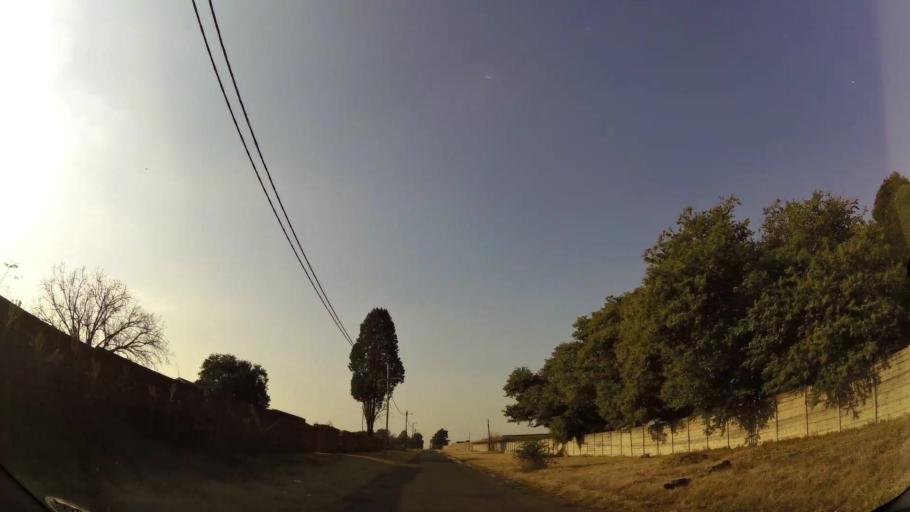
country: ZA
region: Gauteng
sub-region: Ekurhuleni Metropolitan Municipality
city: Benoni
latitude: -26.1454
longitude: 28.3696
